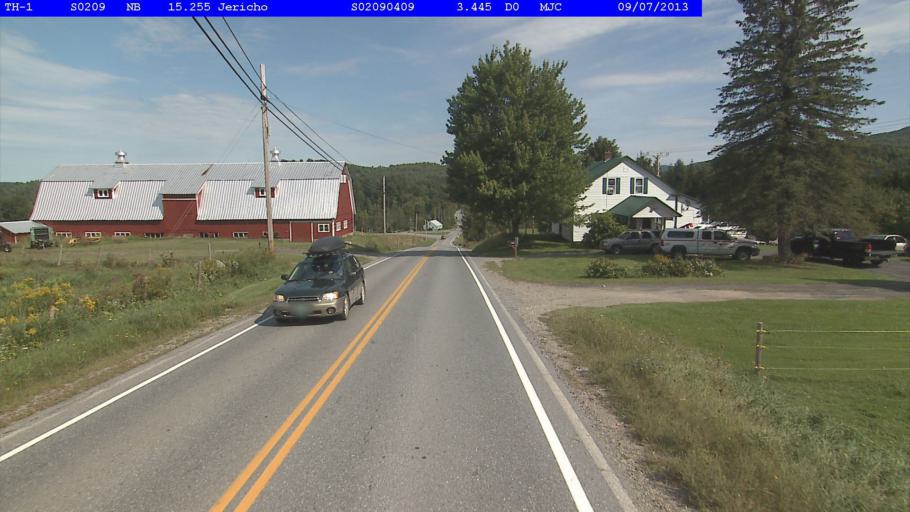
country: US
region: Vermont
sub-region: Chittenden County
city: Jericho
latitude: 44.4772
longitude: -72.9678
